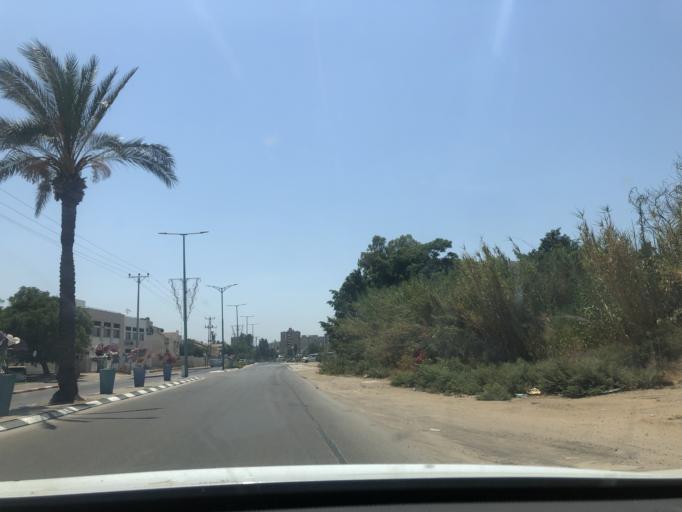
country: IL
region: Central District
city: Lod
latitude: 31.9485
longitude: 34.9020
